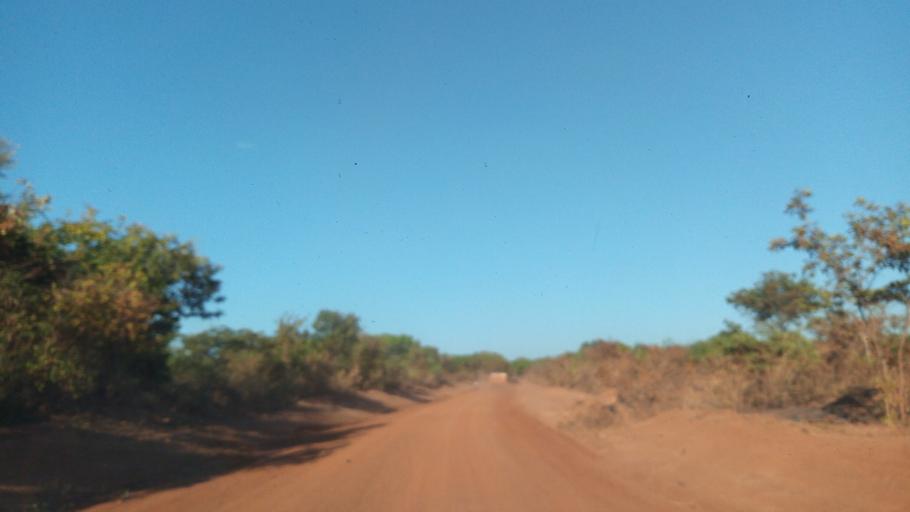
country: ZM
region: Luapula
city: Mwense
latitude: -10.4365
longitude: 28.5941
